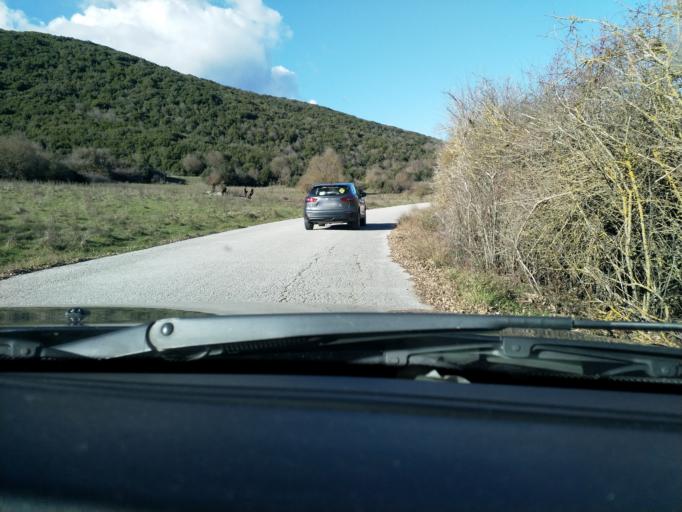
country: GR
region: Epirus
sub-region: Nomos Ioanninon
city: Kalpaki
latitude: 39.8840
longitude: 20.6739
